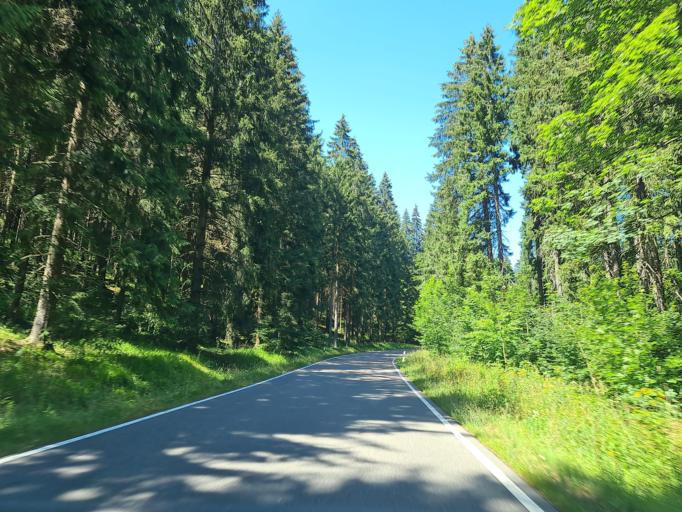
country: DE
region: Saxony
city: Rechenberg-Bienenmuhle
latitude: 50.7112
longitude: 13.5414
